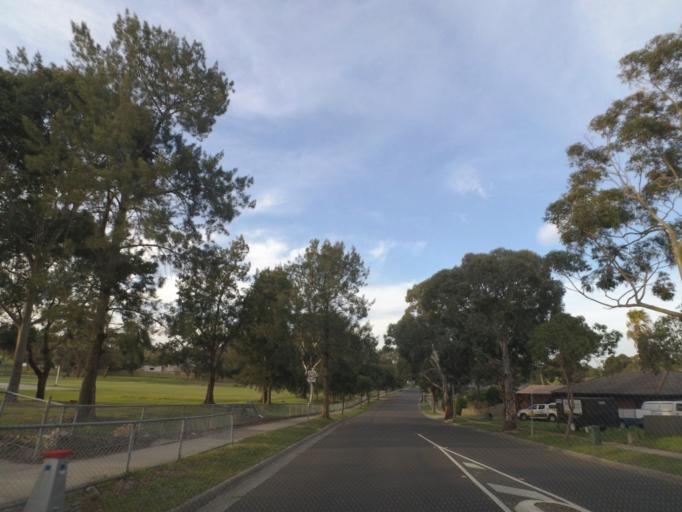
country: AU
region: Victoria
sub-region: Knox
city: Wantirna
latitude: -37.8577
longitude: 145.2319
